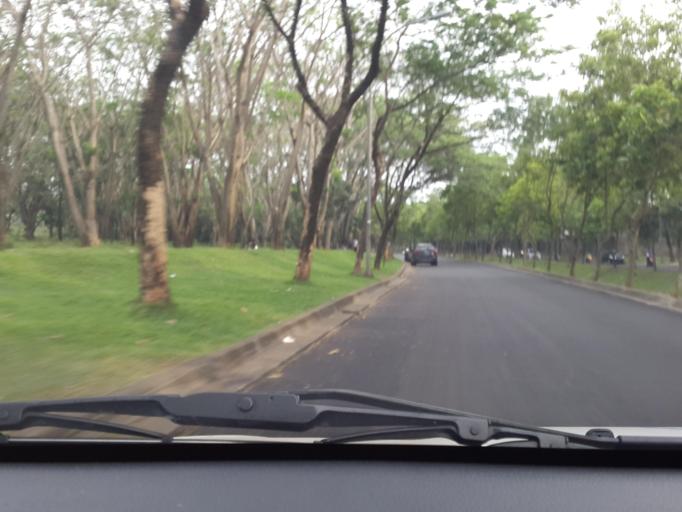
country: ID
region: Banten
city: South Tangerang
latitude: -6.2751
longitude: 106.6996
